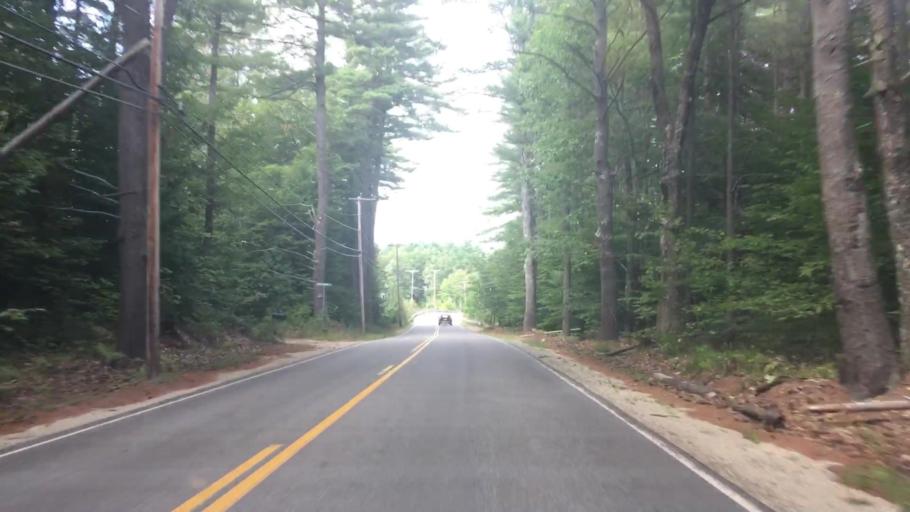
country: US
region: Maine
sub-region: Oxford County
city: Oxford
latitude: 44.1198
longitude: -70.5055
